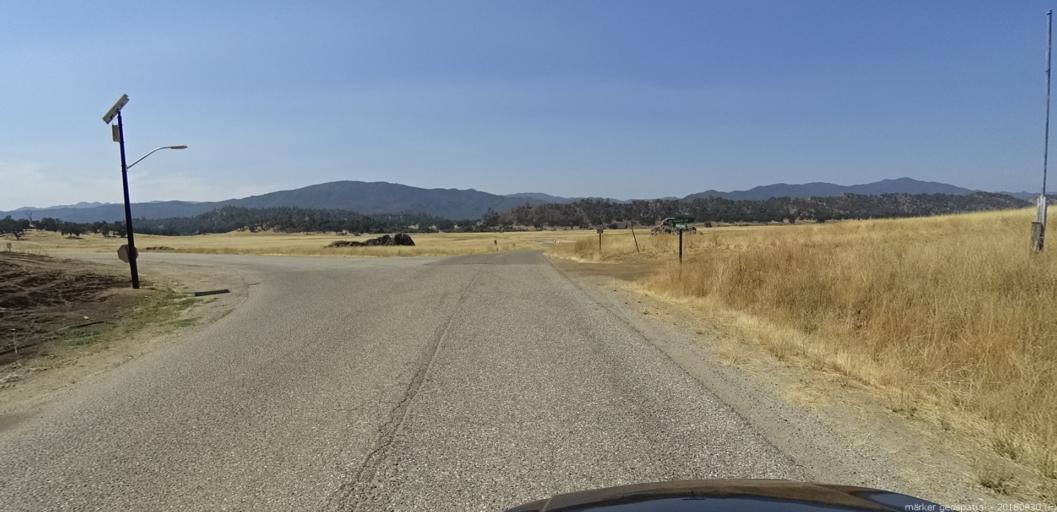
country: US
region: California
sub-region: Monterey County
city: King City
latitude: 35.9760
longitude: -121.2640
